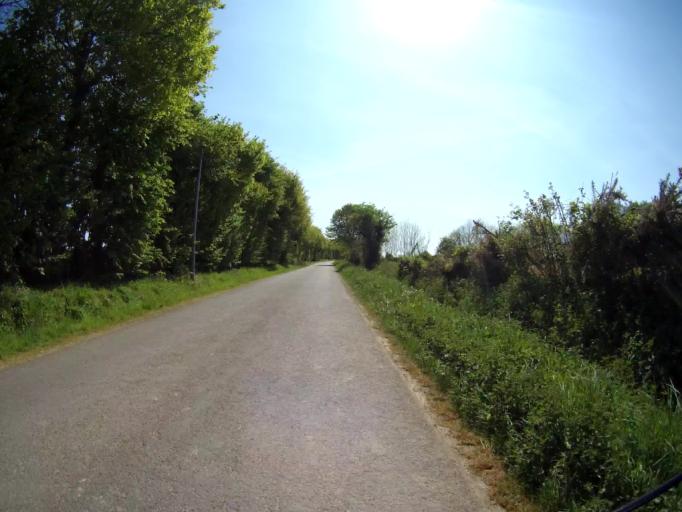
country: FR
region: Brittany
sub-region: Departement d'Ille-et-Vilaine
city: Saint-Erblon
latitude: 48.0237
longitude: -1.6295
